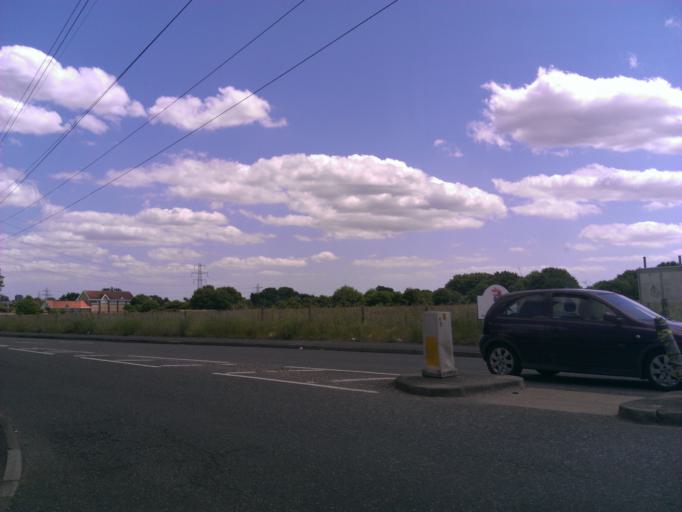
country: GB
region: England
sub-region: Essex
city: Colchester
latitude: 51.8721
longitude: 0.9094
